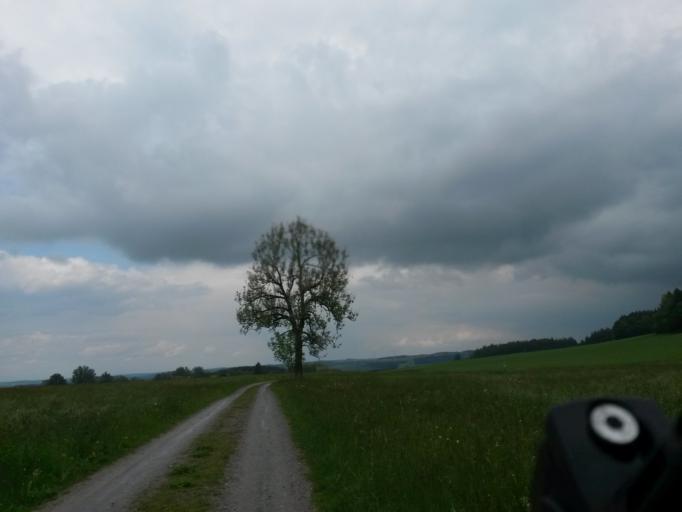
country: DE
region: Baden-Wuerttemberg
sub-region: Tuebingen Region
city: Bad Wurzach
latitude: 47.9265
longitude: 9.8369
